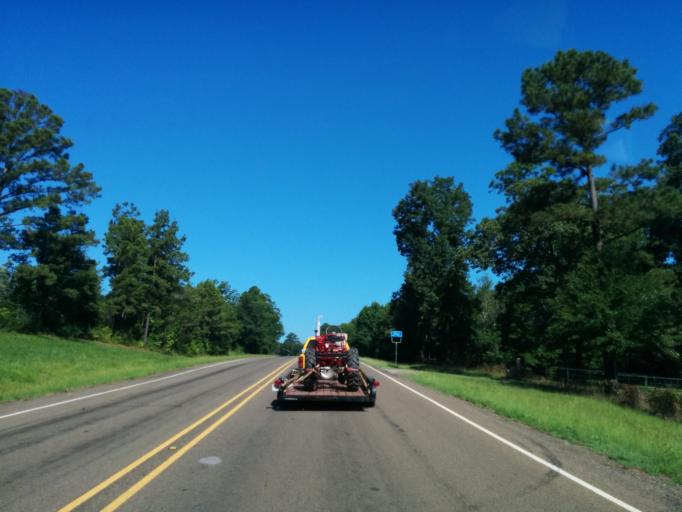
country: US
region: Texas
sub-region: Sabine County
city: Milam
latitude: 31.4306
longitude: -93.8157
